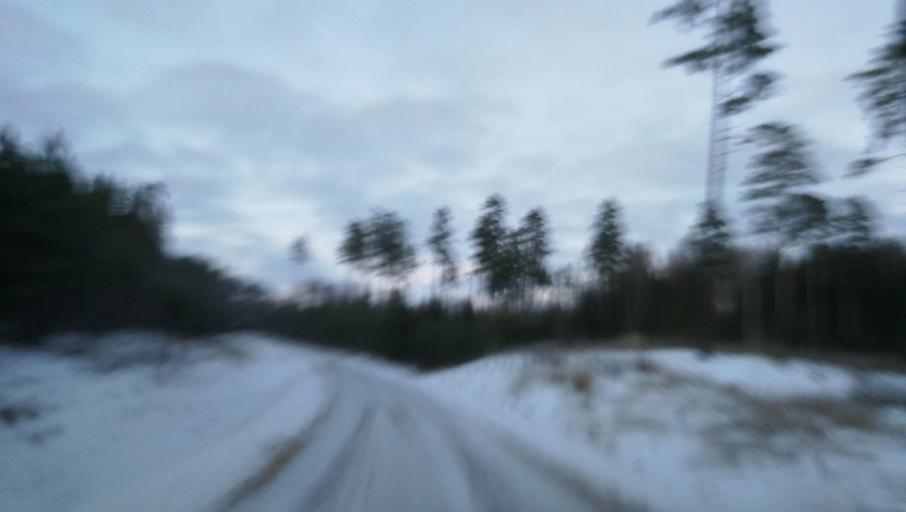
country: LV
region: Amatas Novads
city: Drabesi
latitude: 57.2157
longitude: 25.2872
